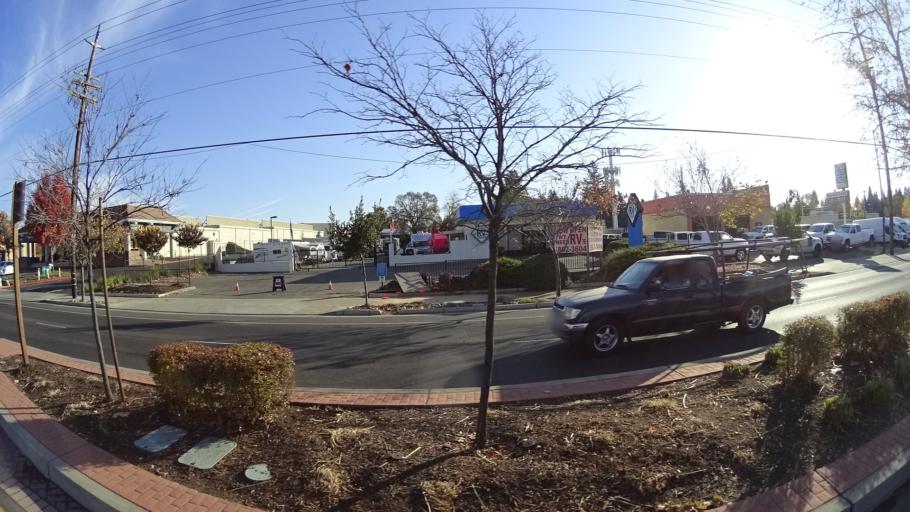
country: US
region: California
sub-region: Sacramento County
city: Citrus Heights
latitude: 38.7059
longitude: -121.2718
